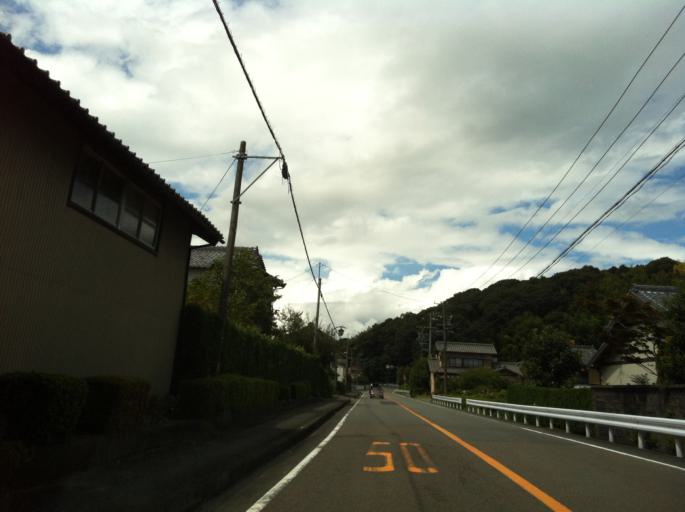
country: JP
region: Shizuoka
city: Kakegawa
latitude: 34.7281
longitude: 138.0443
